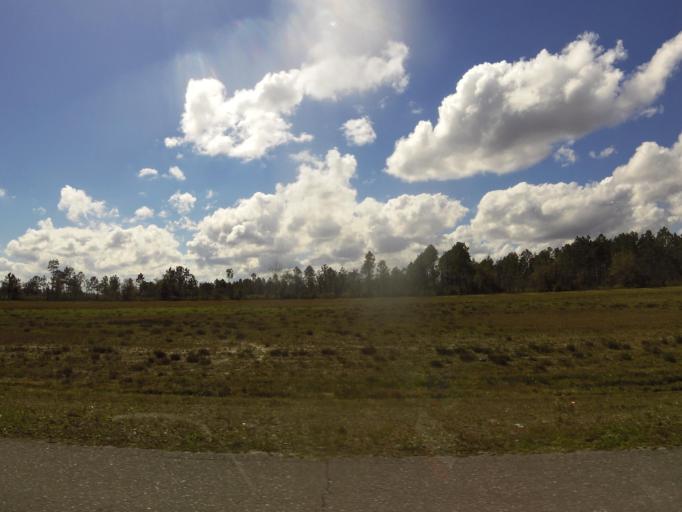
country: US
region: Florida
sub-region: Clay County
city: Green Cove Springs
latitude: 29.8680
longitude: -81.6860
